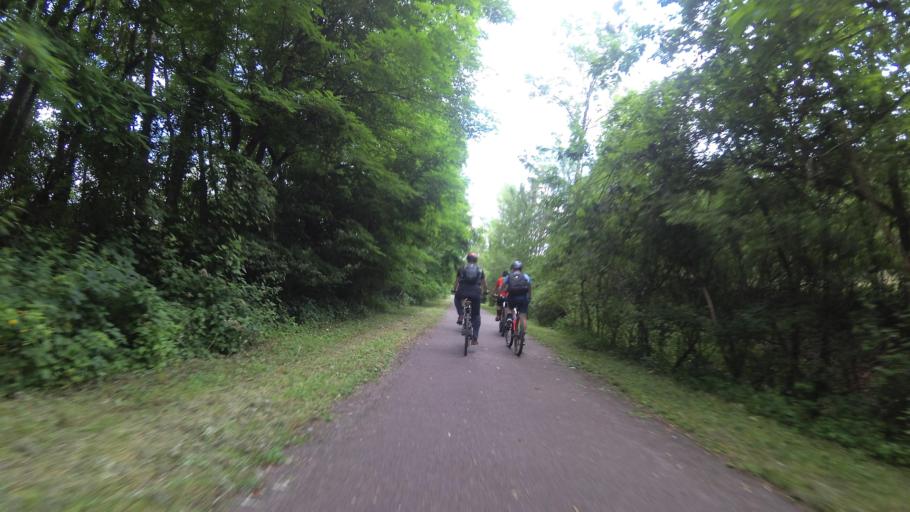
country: FR
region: Lorraine
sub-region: Departement de la Moselle
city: Bliesbruck
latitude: 49.1147
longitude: 7.1656
